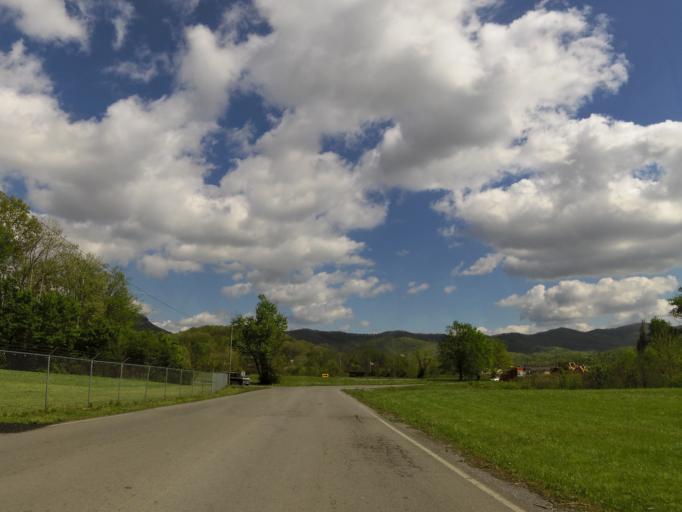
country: US
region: Kentucky
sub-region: Bell County
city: Middlesboro
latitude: 36.6175
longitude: -83.7083
